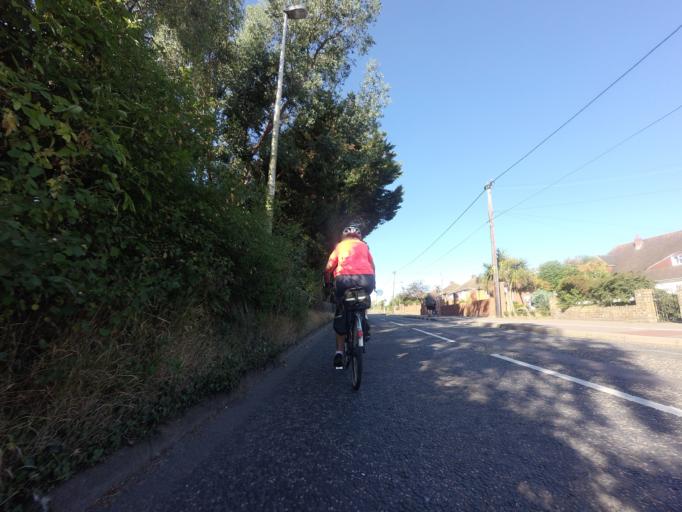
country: GB
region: England
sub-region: Kent
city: Strood
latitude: 51.4106
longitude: 0.5046
